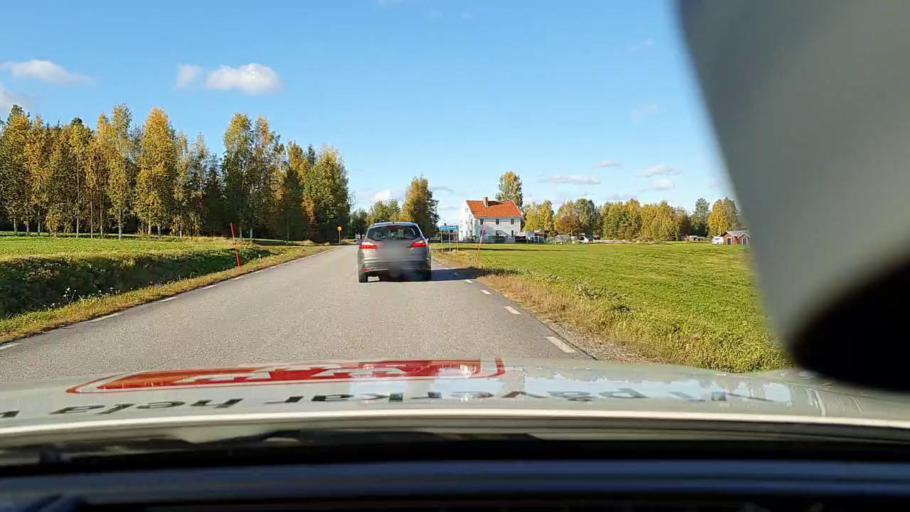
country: SE
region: Norrbotten
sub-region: Pitea Kommun
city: Norrfjarden
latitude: 65.5145
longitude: 21.4956
